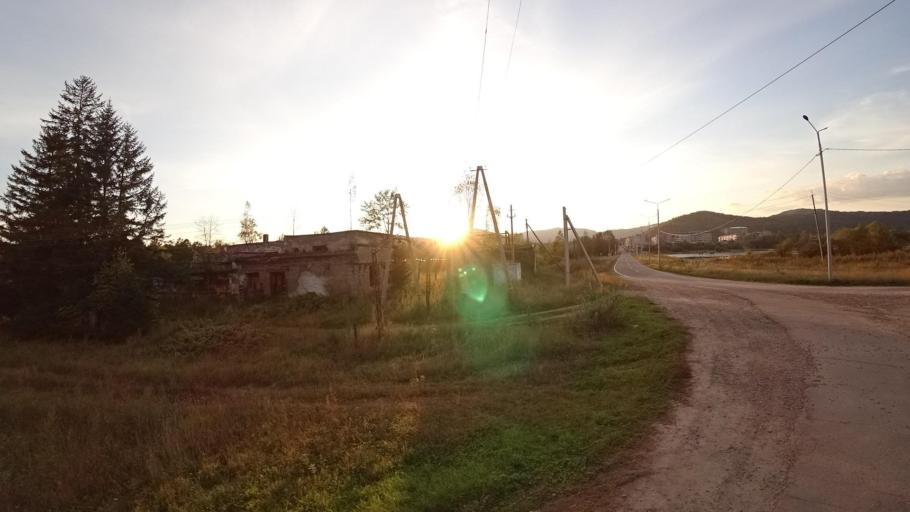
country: RU
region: Jewish Autonomous Oblast
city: Kul'dur
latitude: 49.1988
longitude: 131.6324
